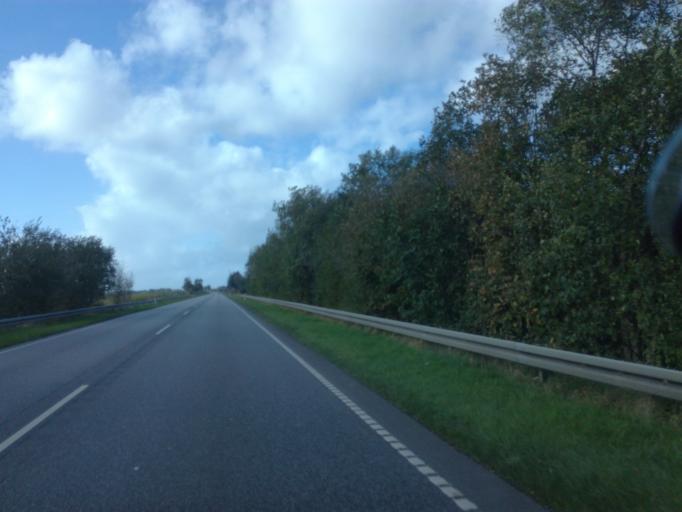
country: DK
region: South Denmark
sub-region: Vejle Kommune
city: Brejning
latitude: 55.6269
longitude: 9.7197
